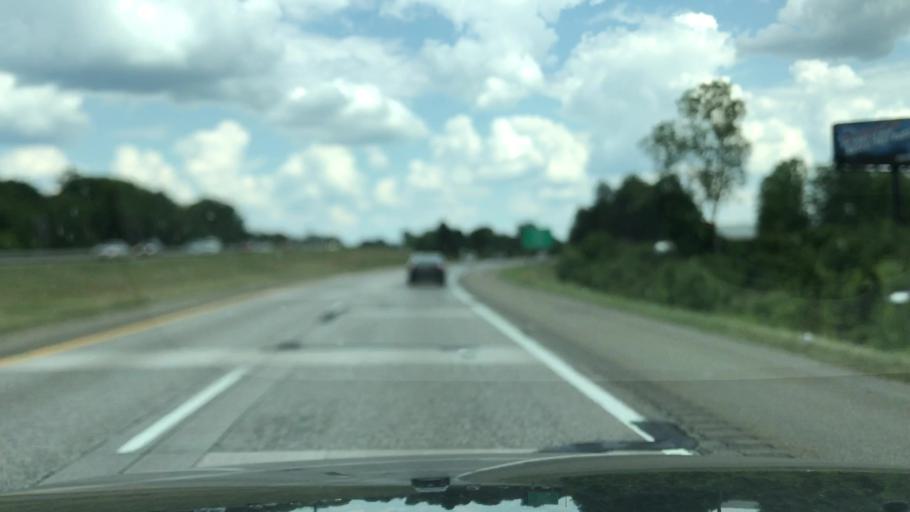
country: US
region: Michigan
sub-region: Kent County
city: East Grand Rapids
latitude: 42.9768
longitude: -85.6083
